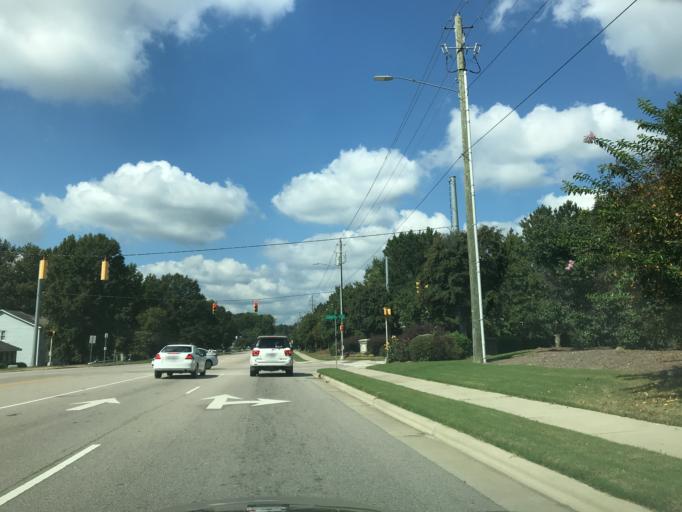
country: US
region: North Carolina
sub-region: Wake County
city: Rolesville
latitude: 35.8857
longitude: -78.5535
